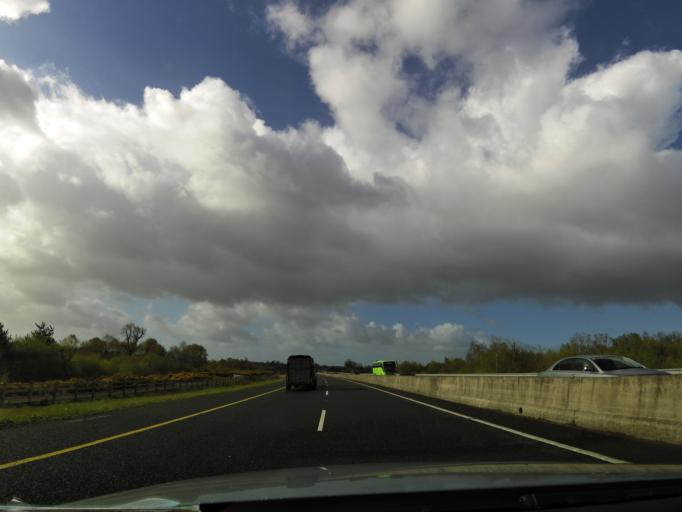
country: IE
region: Munster
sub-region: County Limerick
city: Castleconnell
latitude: 52.6905
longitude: -8.4987
